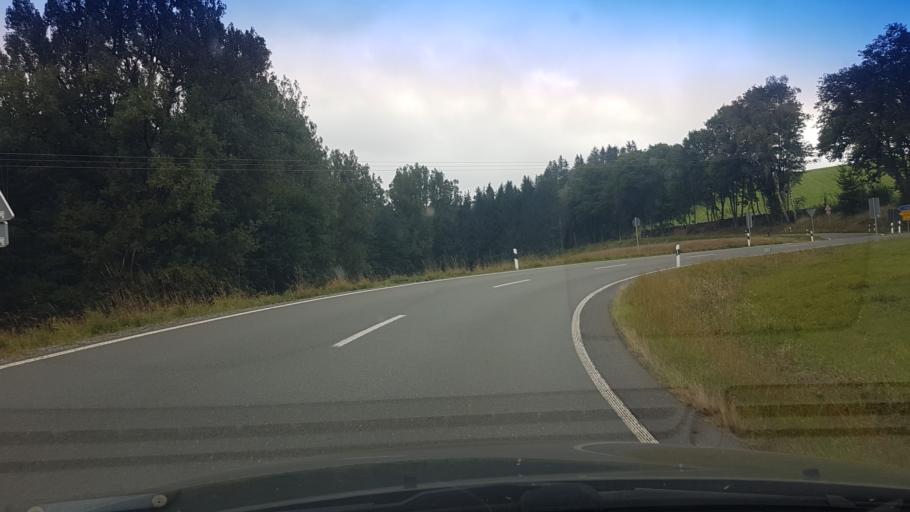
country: DE
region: Bavaria
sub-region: Upper Franconia
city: Bad Berneck im Fichtelgebirge
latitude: 50.0653
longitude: 11.6733
